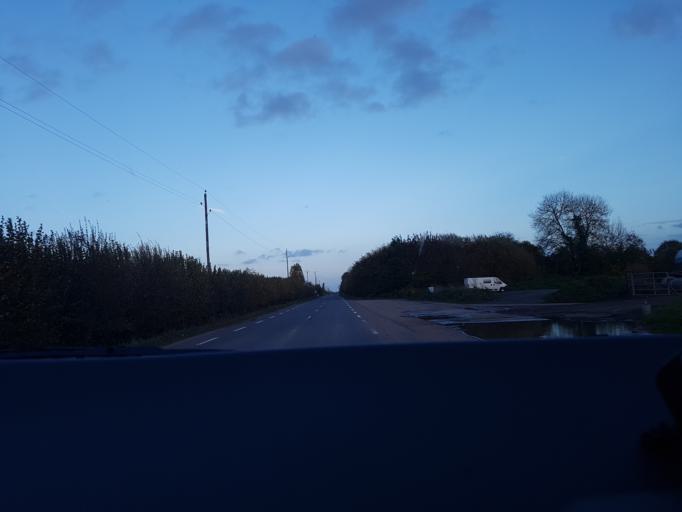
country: FR
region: Lower Normandy
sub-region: Departement du Calvados
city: Touques
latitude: 49.2630
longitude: 0.1321
